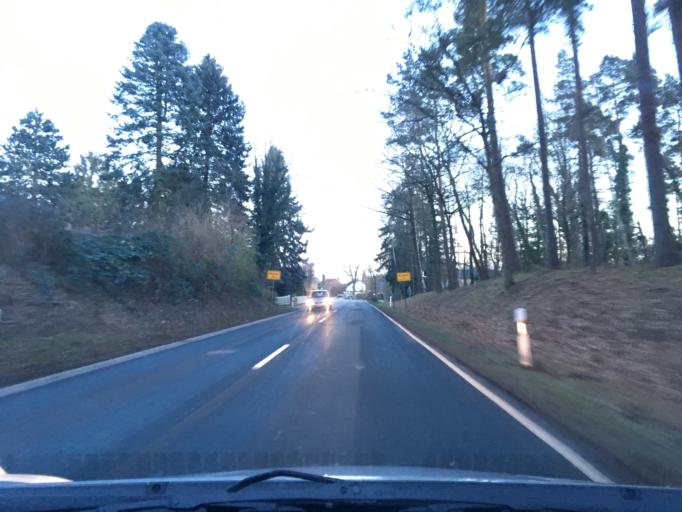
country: DE
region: Lower Saxony
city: Kusten
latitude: 52.9787
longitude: 11.0593
